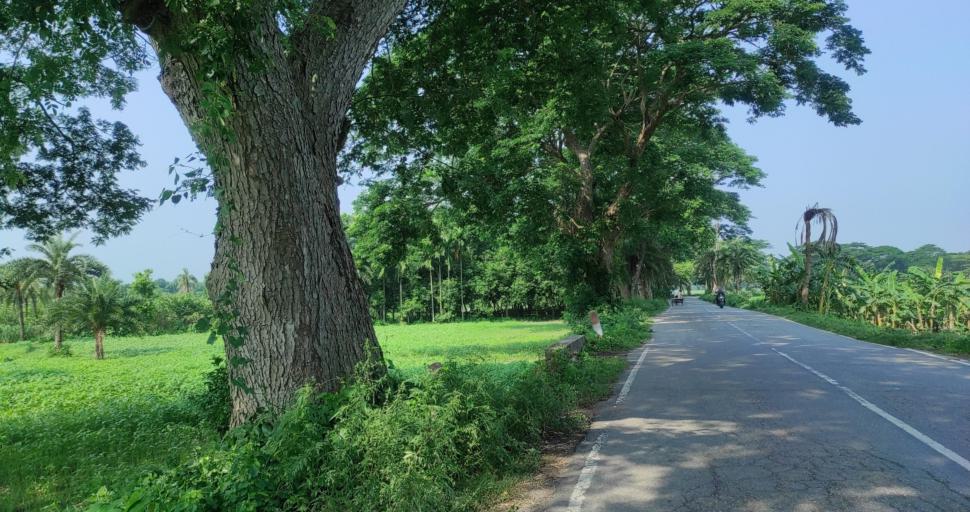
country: BD
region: Rajshahi
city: Ishurdi
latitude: 24.2794
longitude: 89.0639
